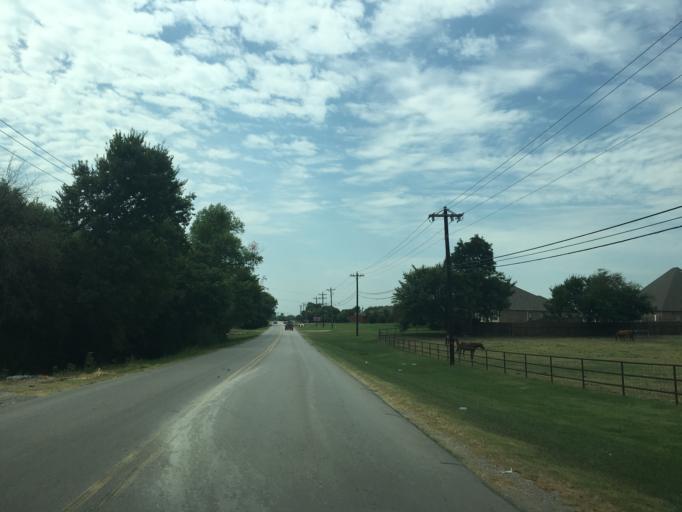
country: US
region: Texas
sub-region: Collin County
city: Wylie
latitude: 32.9972
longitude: -96.5218
